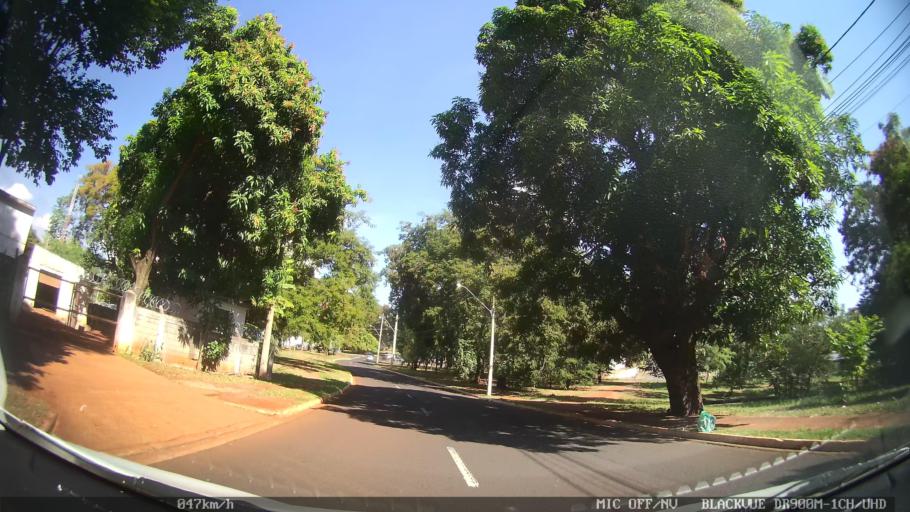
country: BR
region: Sao Paulo
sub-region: Ribeirao Preto
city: Ribeirao Preto
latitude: -21.2121
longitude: -47.8197
